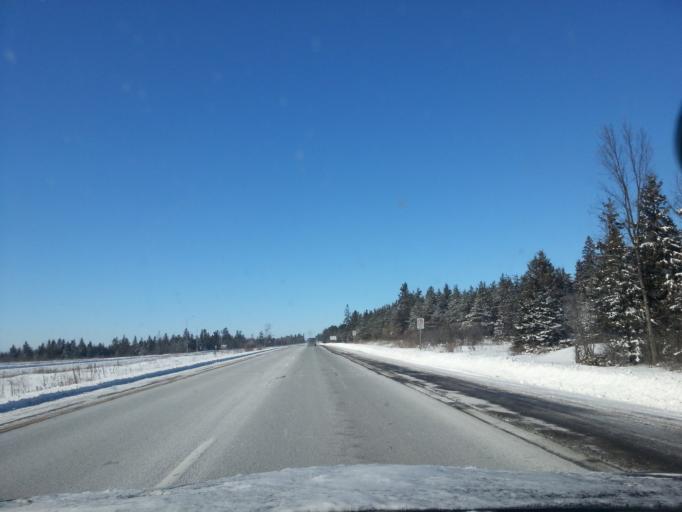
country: CA
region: Ontario
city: Carleton Place
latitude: 45.3335
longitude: -76.1648
